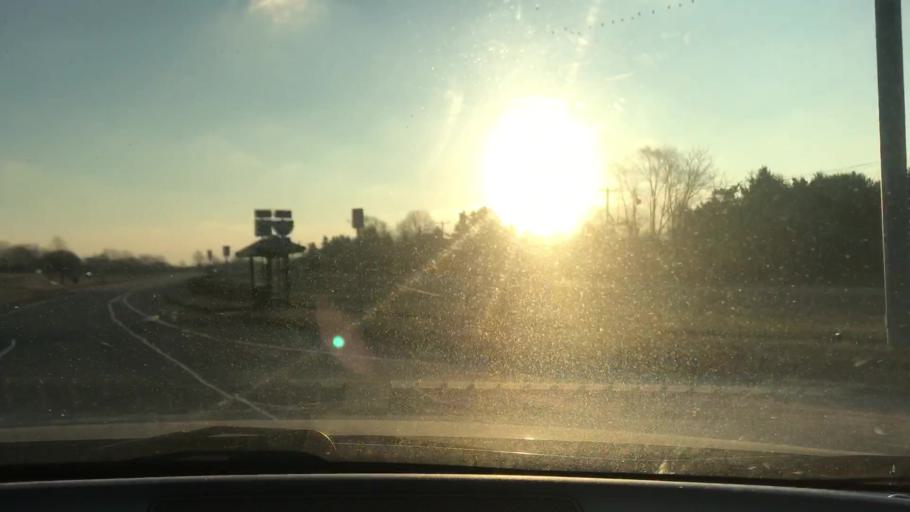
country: US
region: New York
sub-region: Suffolk County
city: Calverton
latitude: 40.9254
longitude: -72.7357
